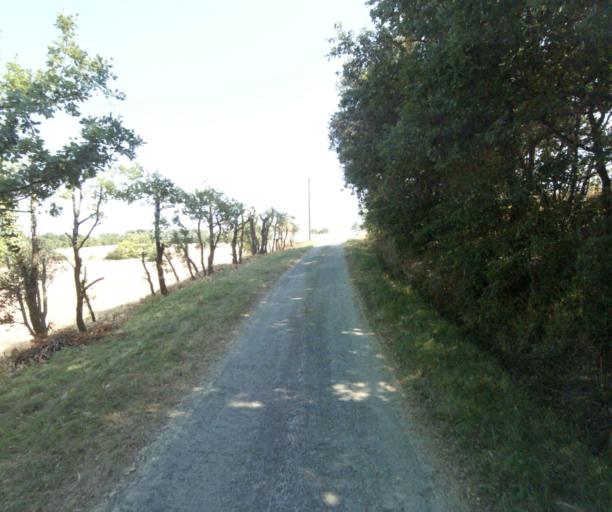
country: FR
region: Midi-Pyrenees
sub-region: Departement de la Haute-Garonne
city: Saint-Felix-Lauragais
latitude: 43.4286
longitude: 1.8290
